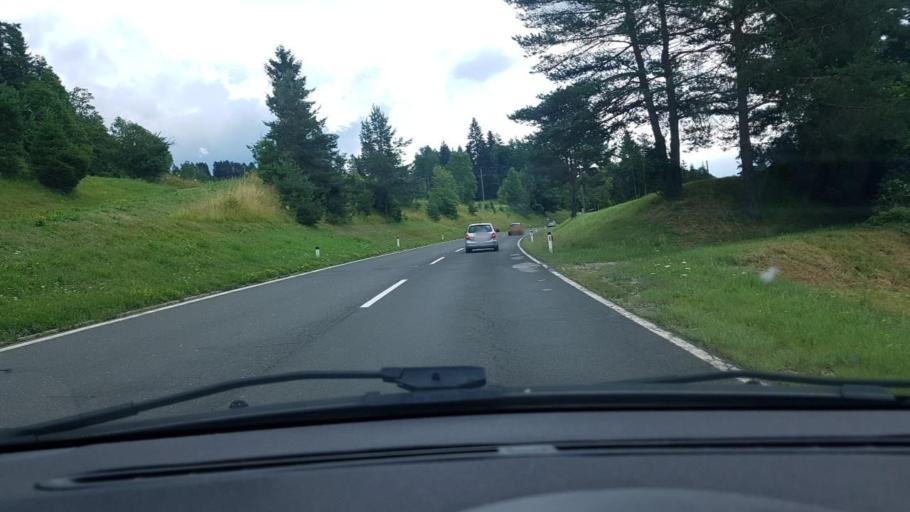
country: AT
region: Carinthia
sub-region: Politischer Bezirk Villach Land
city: Stockenboi
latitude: 46.6281
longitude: 13.4798
